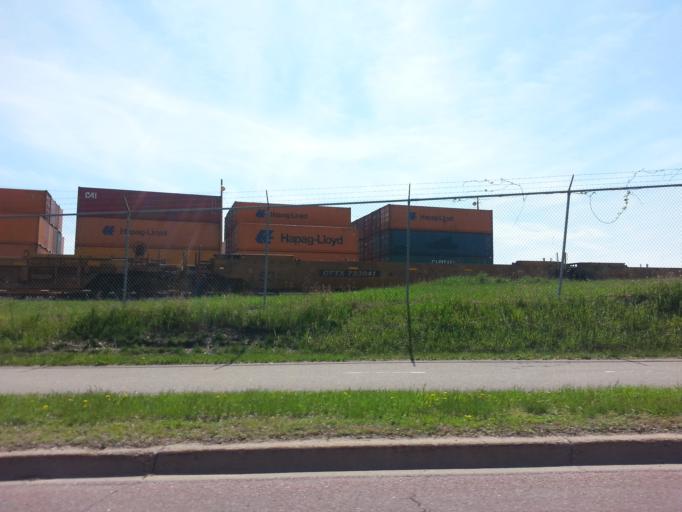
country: US
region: Minnesota
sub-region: Anoka County
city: Columbia Heights
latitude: 45.0252
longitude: -93.2591
